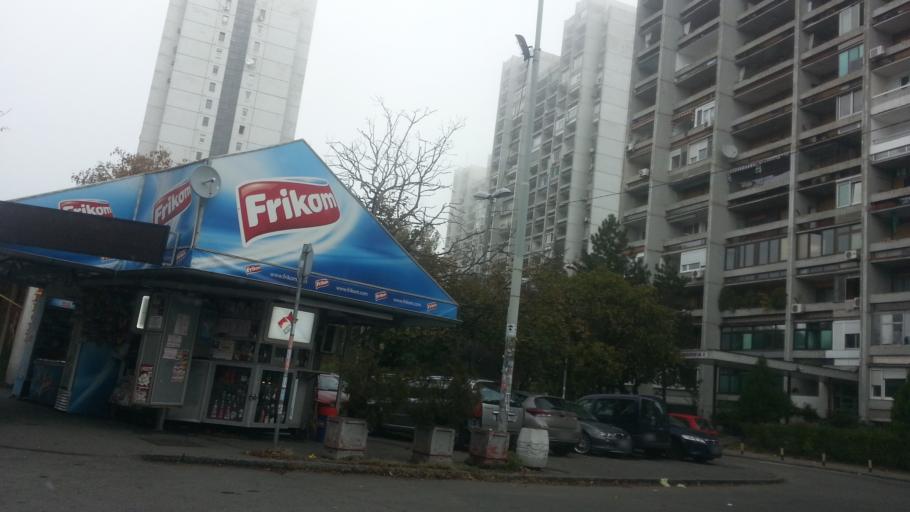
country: RS
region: Central Serbia
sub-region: Belgrade
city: Zemun
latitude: 44.8390
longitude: 20.4159
